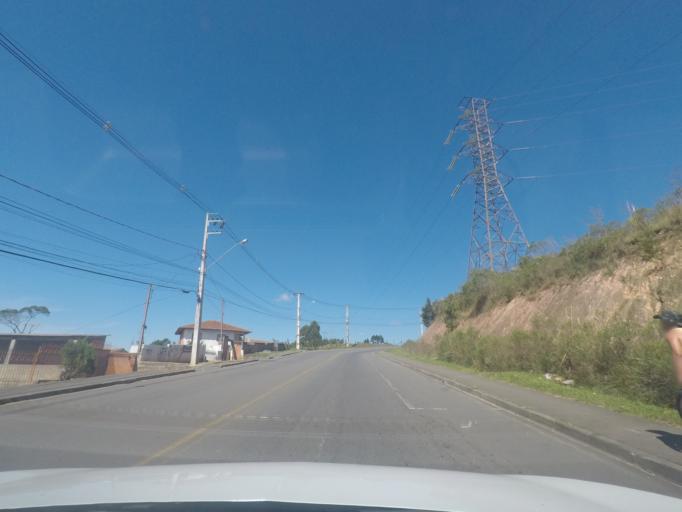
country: BR
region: Parana
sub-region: Almirante Tamandare
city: Almirante Tamandare
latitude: -25.3367
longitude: -49.3066
